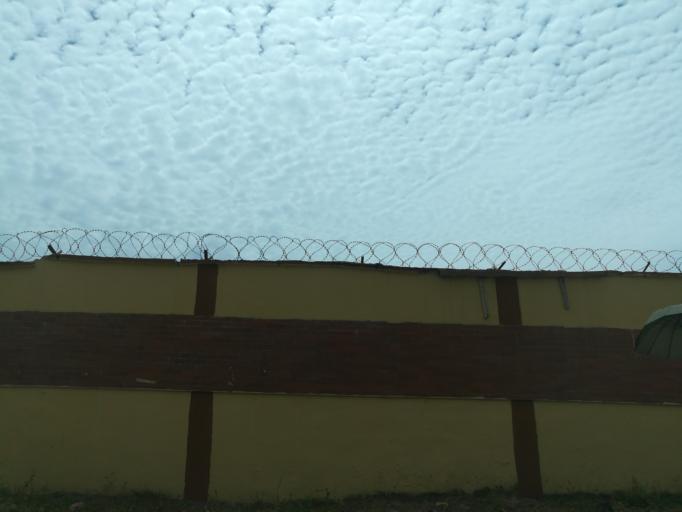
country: NG
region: Lagos
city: Ebute Ikorodu
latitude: 6.5563
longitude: 3.4759
